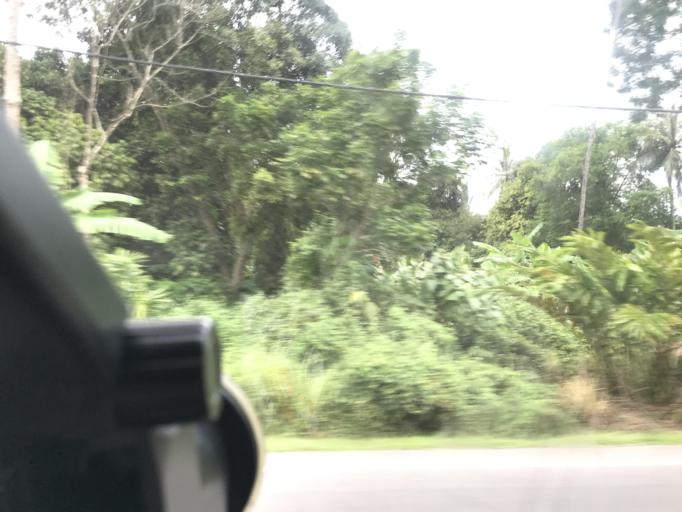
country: MY
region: Kelantan
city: Kota Bharu
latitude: 6.1274
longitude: 102.1750
